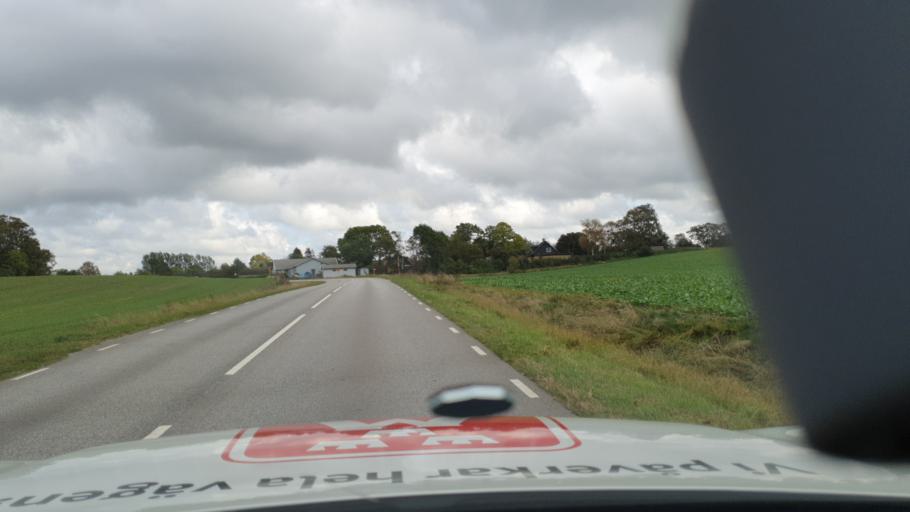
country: SE
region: Skane
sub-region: Svedala Kommun
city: Svedala
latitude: 55.4970
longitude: 13.1803
